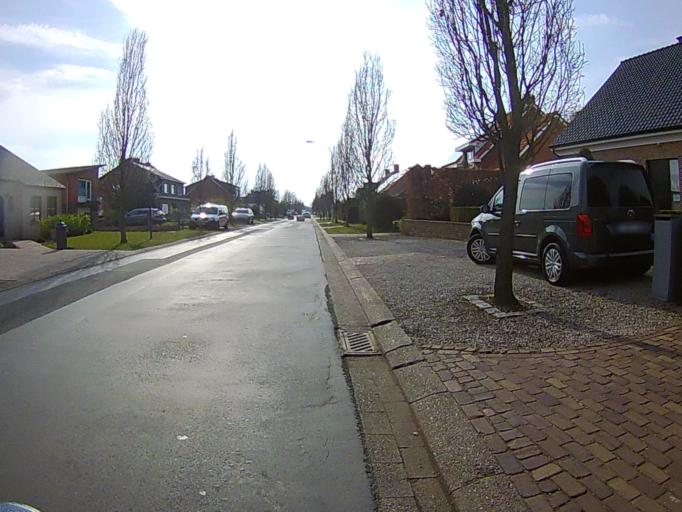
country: BE
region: Flanders
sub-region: Provincie Antwerpen
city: Grobbendonk
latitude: 51.1901
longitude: 4.7268
